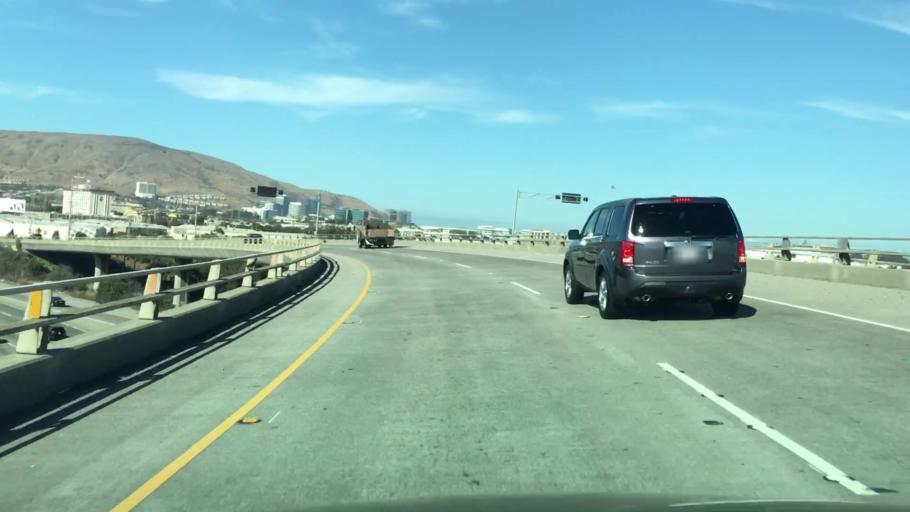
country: US
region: California
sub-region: San Mateo County
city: San Bruno
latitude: 37.6358
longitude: -122.4024
